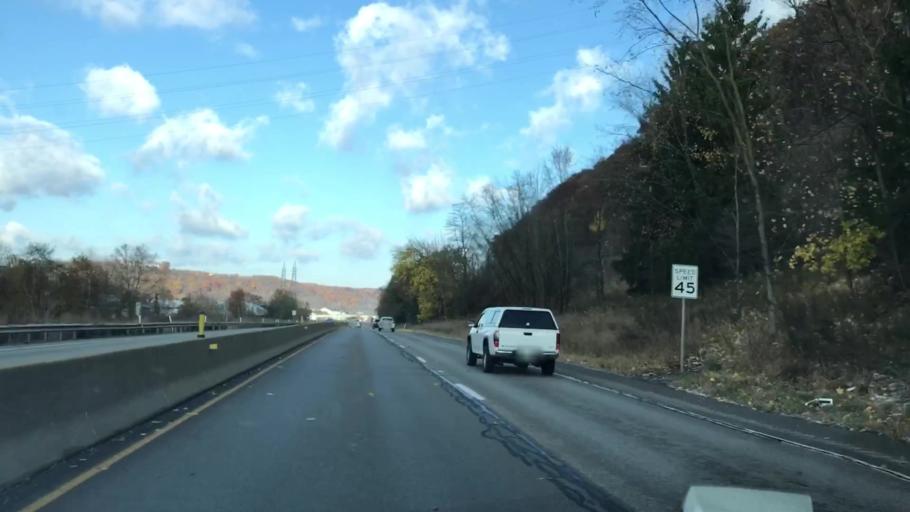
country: US
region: Pennsylvania
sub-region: Allegheny County
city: Leetsdale
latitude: 40.5715
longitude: -80.2169
